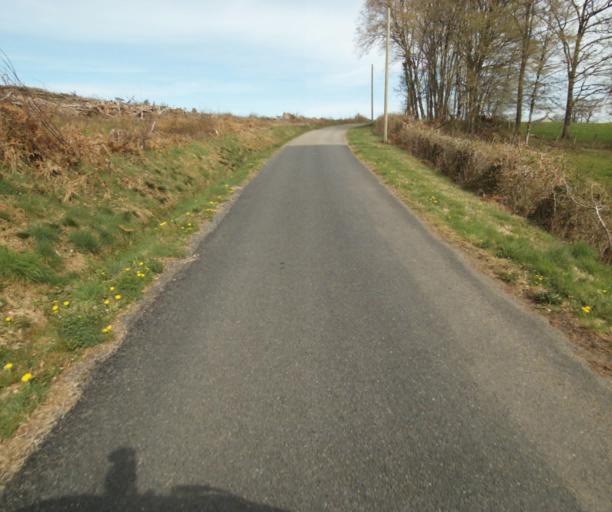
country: FR
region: Limousin
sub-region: Departement de la Correze
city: Correze
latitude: 45.3672
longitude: 1.8191
